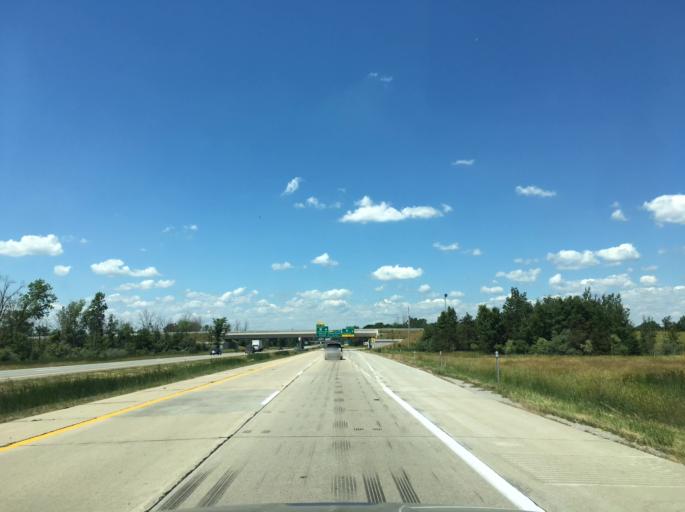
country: US
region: Michigan
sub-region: Bay County
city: Auburn
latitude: 43.5977
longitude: -84.1362
